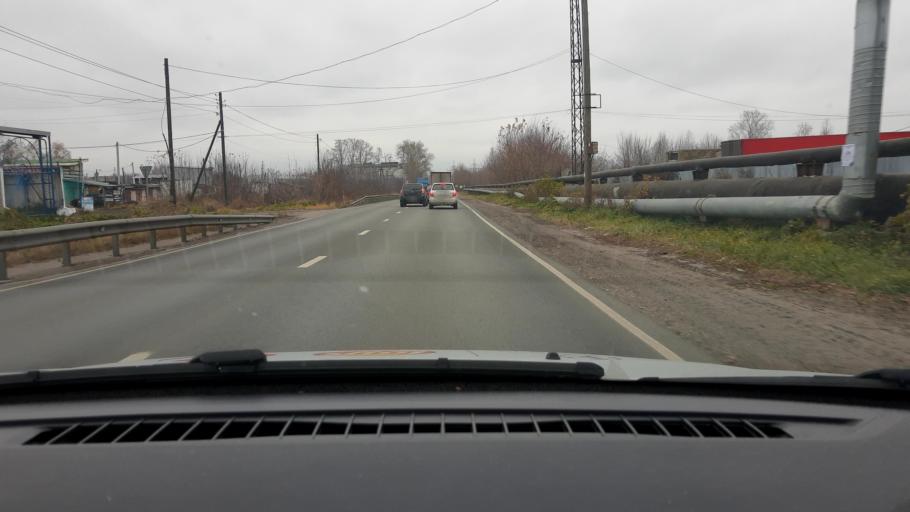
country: RU
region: Nizjnij Novgorod
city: Novaya Balakhna
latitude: 56.4951
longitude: 43.5946
